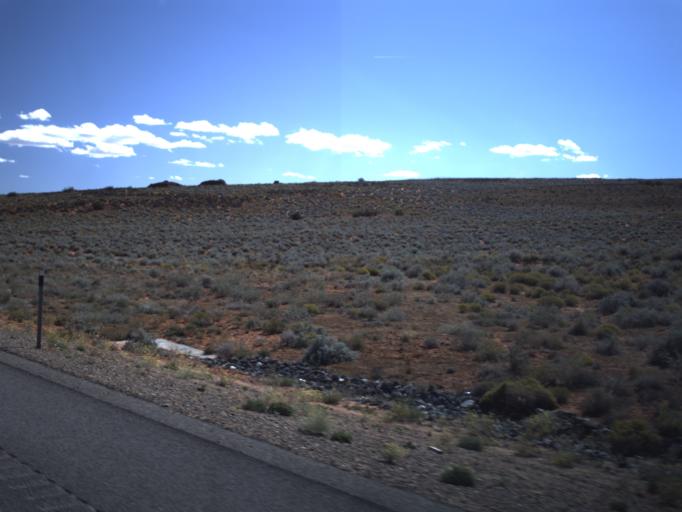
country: US
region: Utah
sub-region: Washington County
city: Washington
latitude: 37.1094
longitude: -113.4077
